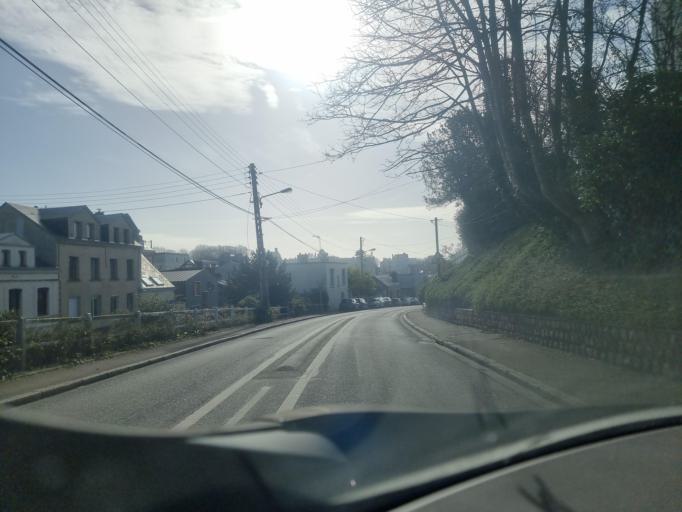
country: FR
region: Haute-Normandie
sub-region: Departement de la Seine-Maritime
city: Le Havre
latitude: 49.5040
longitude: 0.0998
